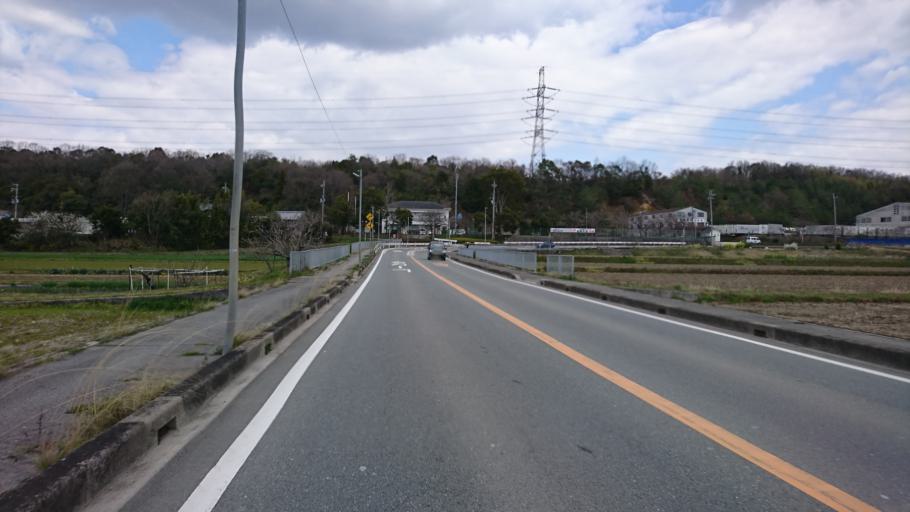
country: JP
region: Hyogo
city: Miki
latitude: 34.7670
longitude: 134.9530
